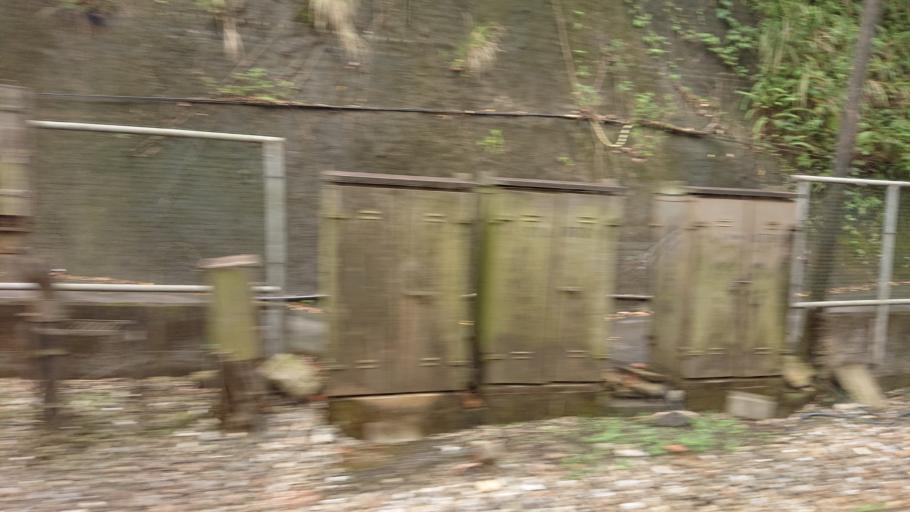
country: TW
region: Taiwan
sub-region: Keelung
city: Keelung
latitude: 25.0576
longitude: 121.8455
